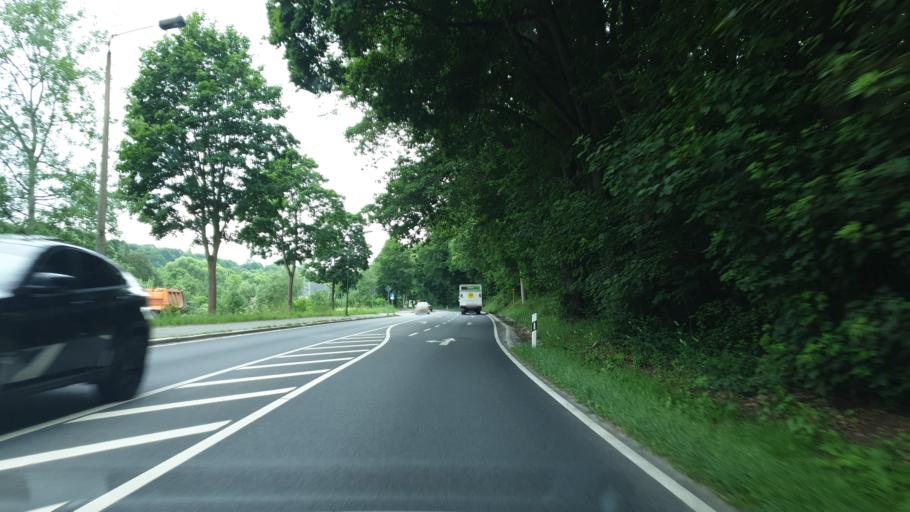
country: DE
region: Saxony
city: Auerbach
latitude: 50.5171
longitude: 12.4009
